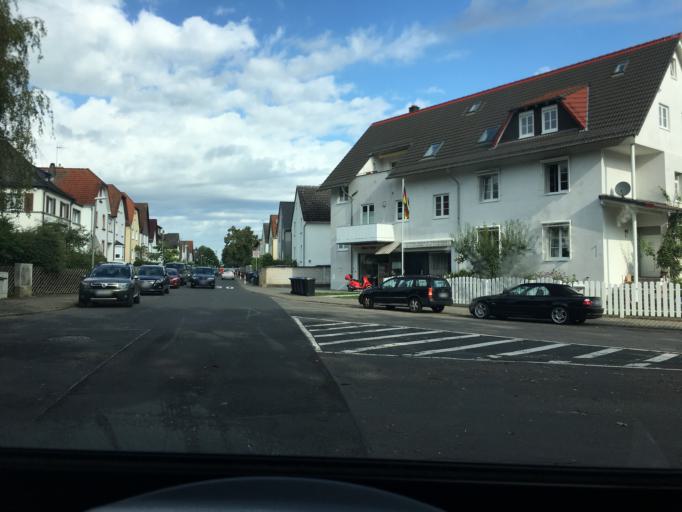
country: DE
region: Hesse
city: Dreieich
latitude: 49.9982
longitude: 8.7066
